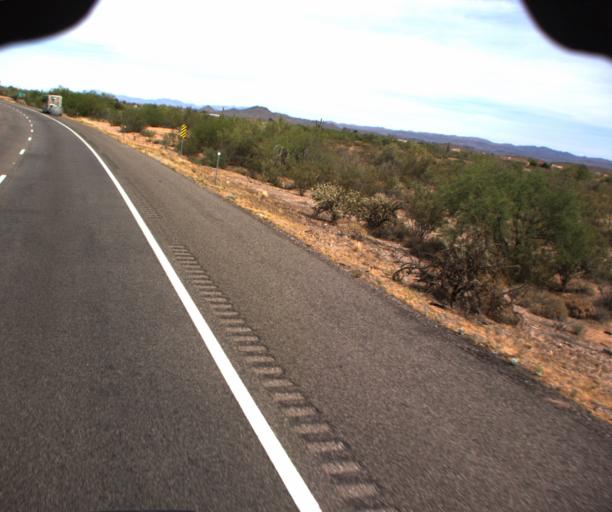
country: US
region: Arizona
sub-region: Maricopa County
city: Wickenburg
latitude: 33.8464
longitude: -112.6124
